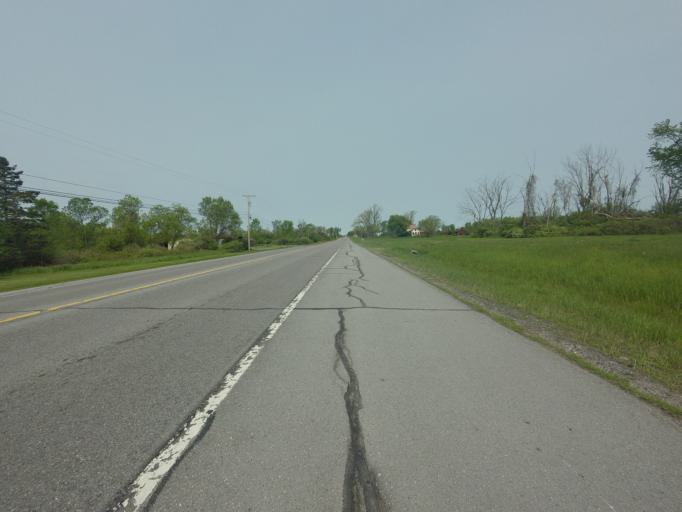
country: US
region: New York
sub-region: Jefferson County
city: Dexter
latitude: 44.0342
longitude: -76.0607
